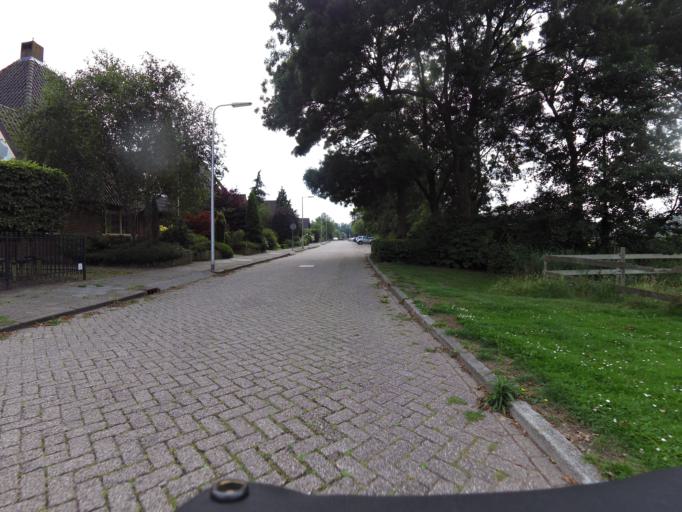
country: NL
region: South Holland
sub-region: Gemeente Maassluis
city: Maassluis
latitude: 51.8850
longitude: 4.2180
